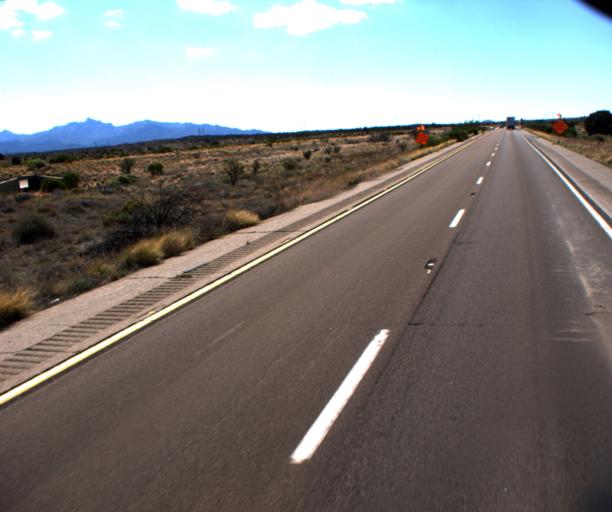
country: US
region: Arizona
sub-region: Mohave County
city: New Kingman-Butler
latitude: 35.1433
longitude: -113.6794
